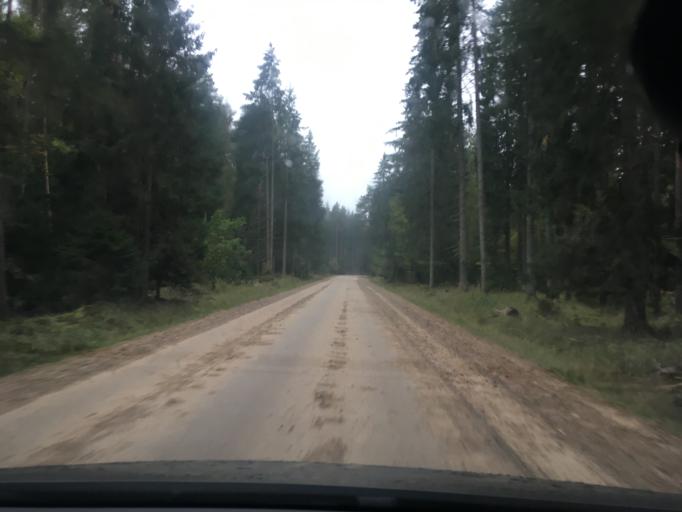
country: LV
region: Kuldigas Rajons
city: Kuldiga
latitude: 56.9978
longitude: 21.9793
